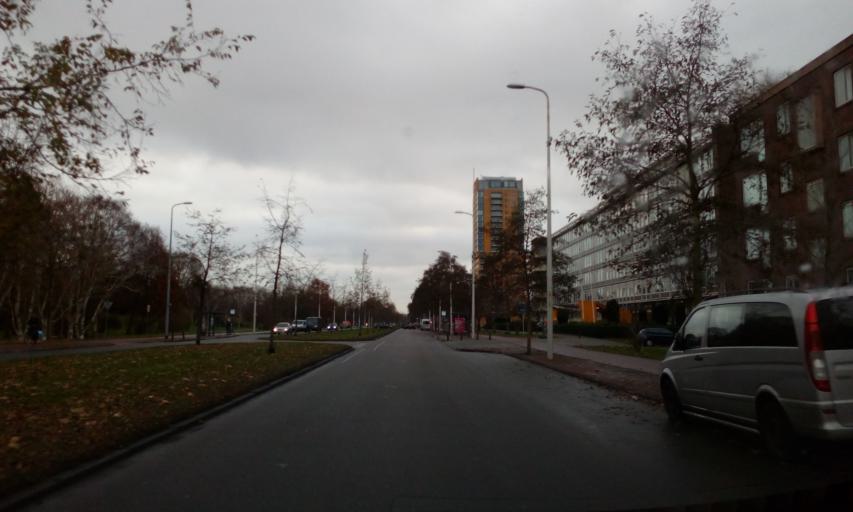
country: NL
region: South Holland
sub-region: Gemeente Den Haag
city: The Hague
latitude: 52.0518
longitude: 4.2797
